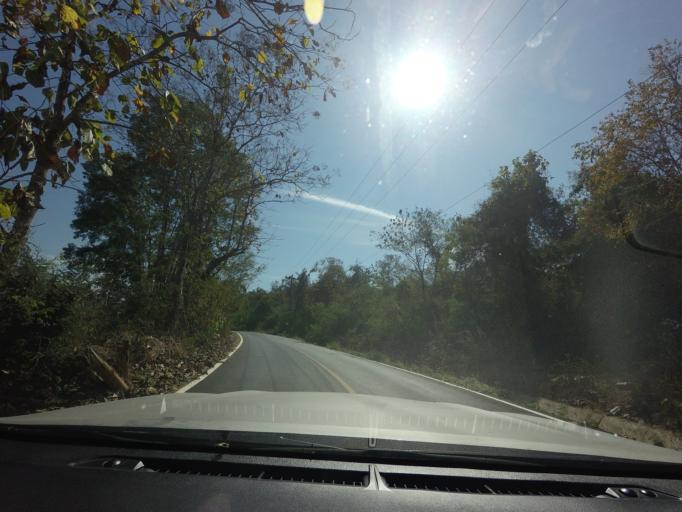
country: TH
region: Mae Hong Son
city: Wiang Nuea
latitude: 19.3782
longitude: 98.4342
